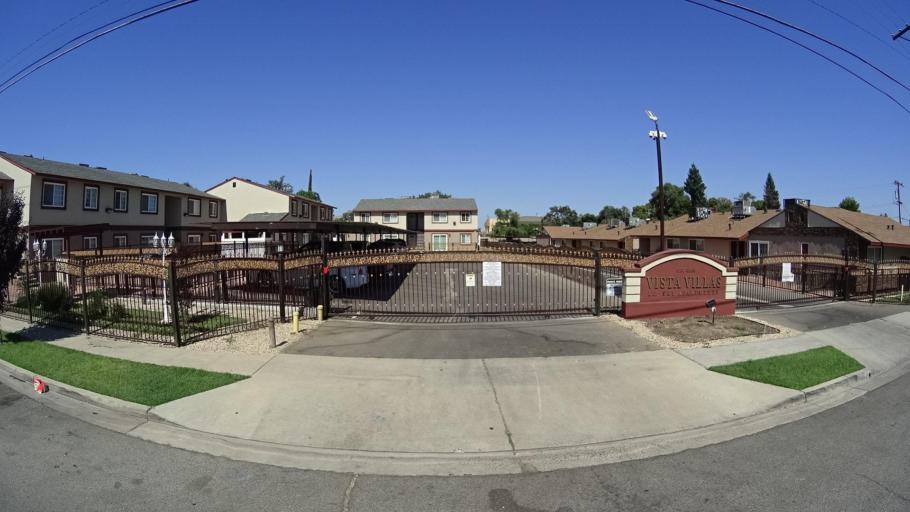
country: US
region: California
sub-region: Fresno County
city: Tarpey Village
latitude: 36.7804
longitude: -119.7408
